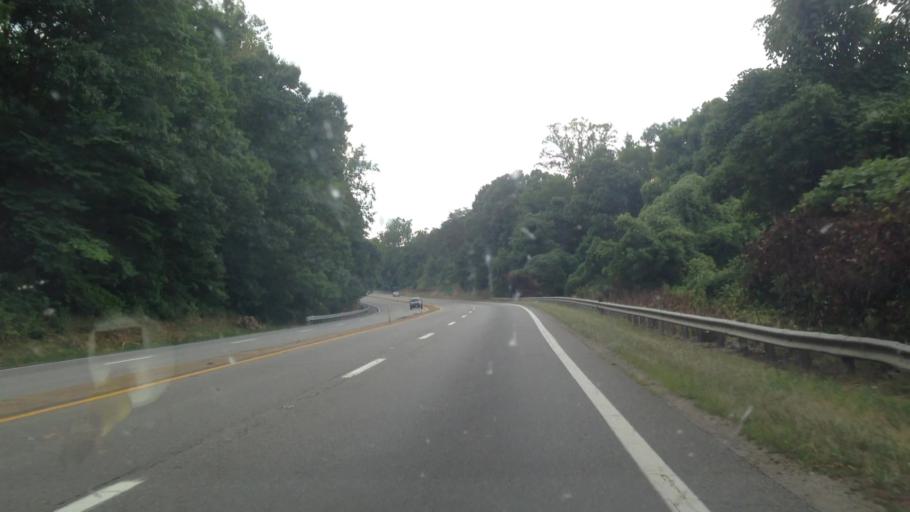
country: US
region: Virginia
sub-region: Henry County
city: Chatmoss
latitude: 36.5769
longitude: -79.8662
